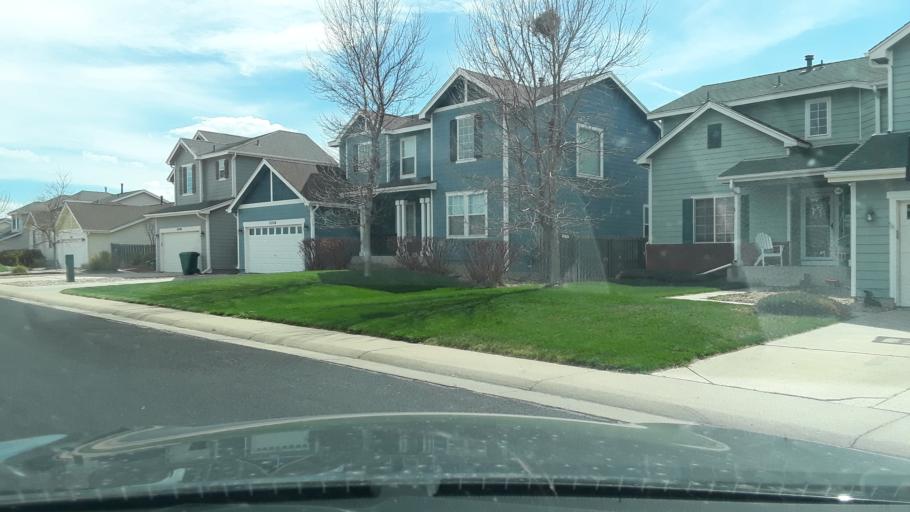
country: US
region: Colorado
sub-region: El Paso County
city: Monument
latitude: 39.0817
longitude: -104.8687
